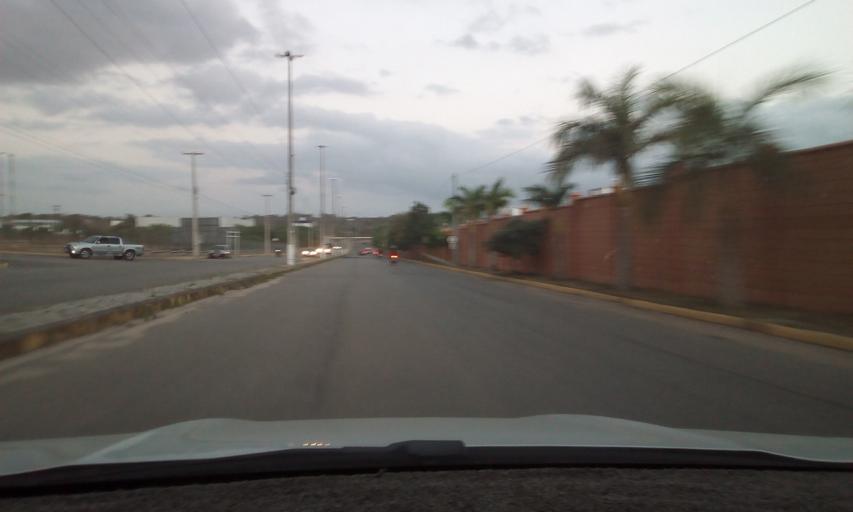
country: BR
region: Pernambuco
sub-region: Caruaru
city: Caruaru
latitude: -8.2421
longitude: -35.9797
